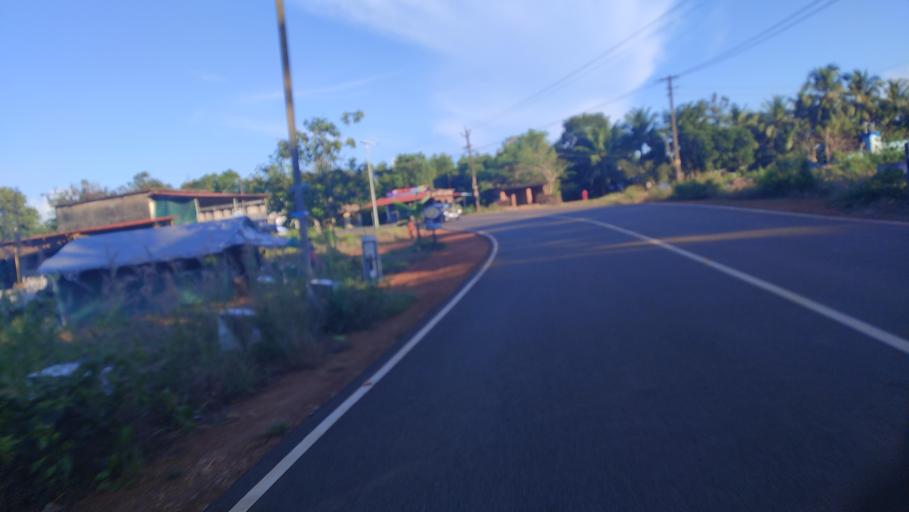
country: IN
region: Kerala
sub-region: Kasaragod District
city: Kasaragod
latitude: 12.4634
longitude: 75.0697
